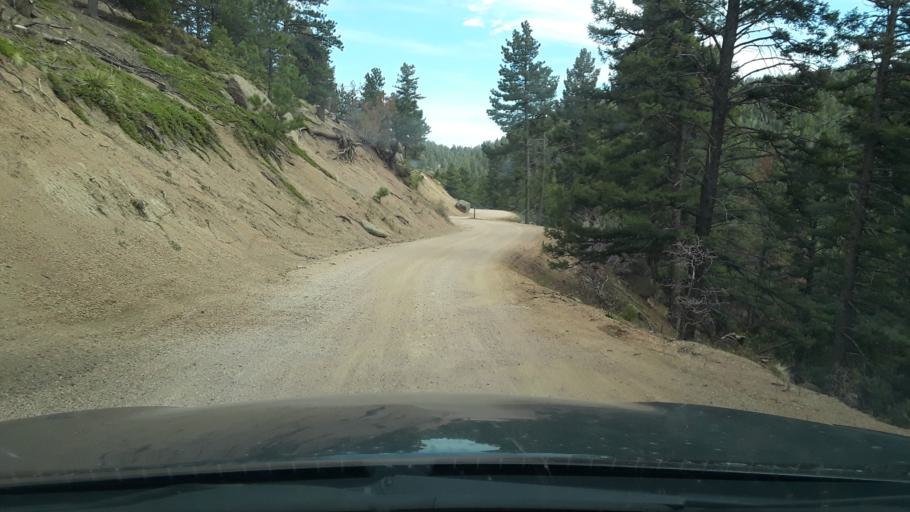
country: US
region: Colorado
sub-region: El Paso County
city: Palmer Lake
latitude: 39.0706
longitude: -104.9354
